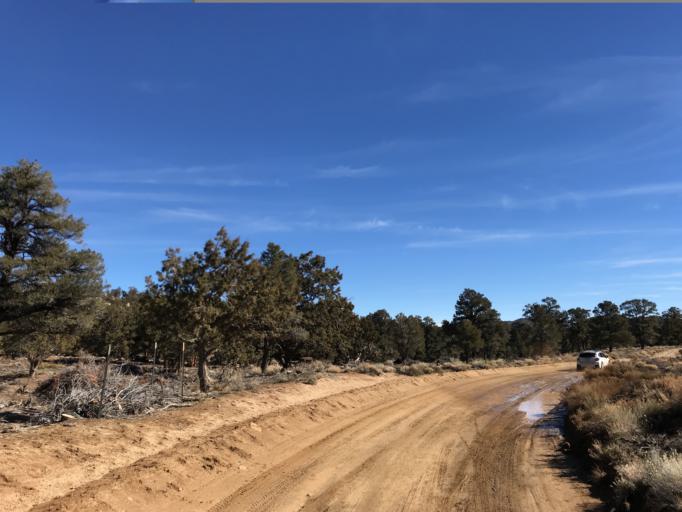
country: US
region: California
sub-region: San Bernardino County
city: Big Bear City
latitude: 34.2693
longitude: -116.7655
